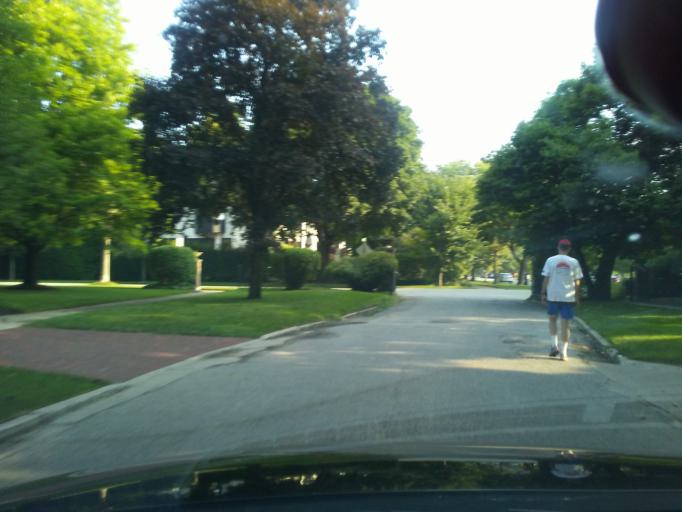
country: US
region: Illinois
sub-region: Cook County
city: Evanston
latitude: 42.0352
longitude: -87.6707
